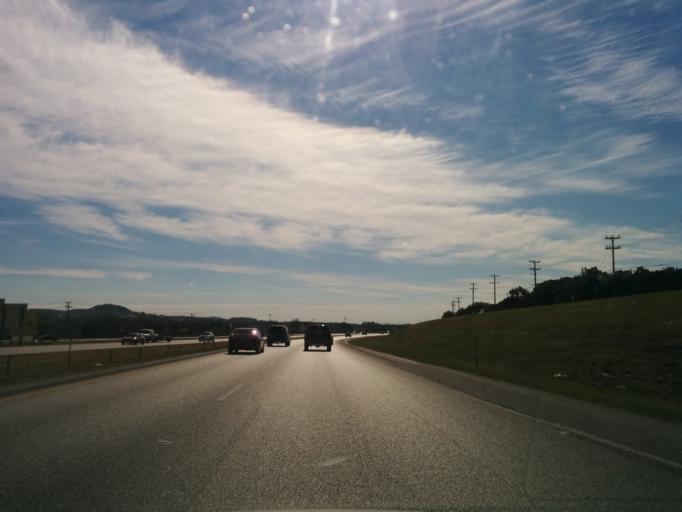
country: US
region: Texas
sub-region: Bexar County
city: Cross Mountain
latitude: 29.6612
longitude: -98.6287
